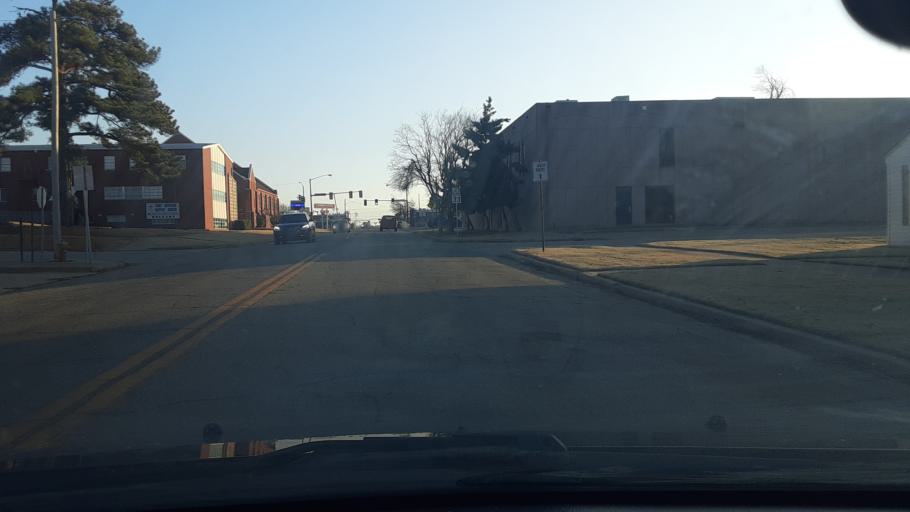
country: US
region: Oklahoma
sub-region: Logan County
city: Guthrie
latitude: 35.8815
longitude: -97.4241
